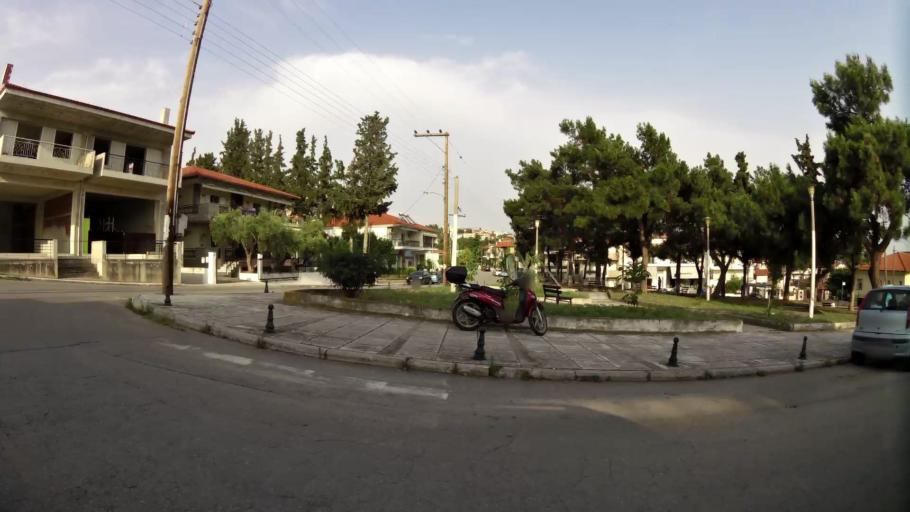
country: GR
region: Central Macedonia
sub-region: Nomos Thessalonikis
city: Oraiokastro
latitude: 40.7236
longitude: 22.9057
